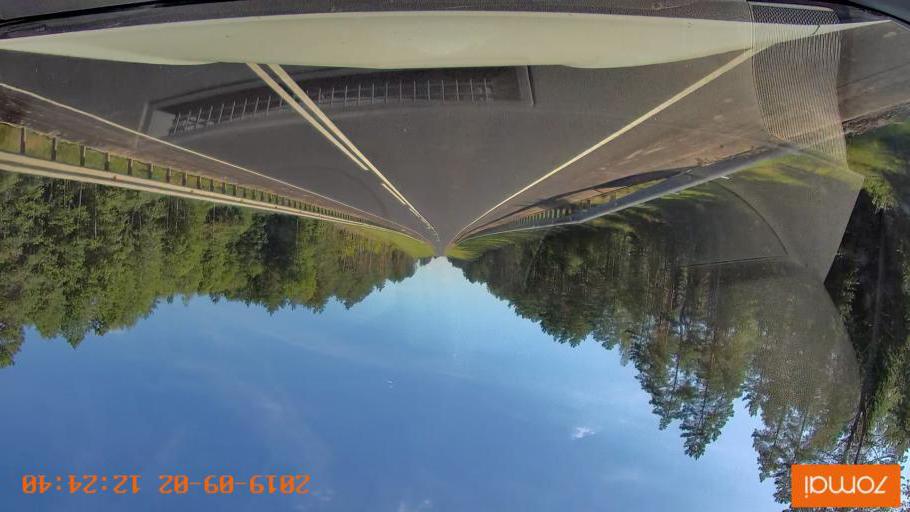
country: RU
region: Smolensk
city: Shumyachi
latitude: 53.8667
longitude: 32.6029
